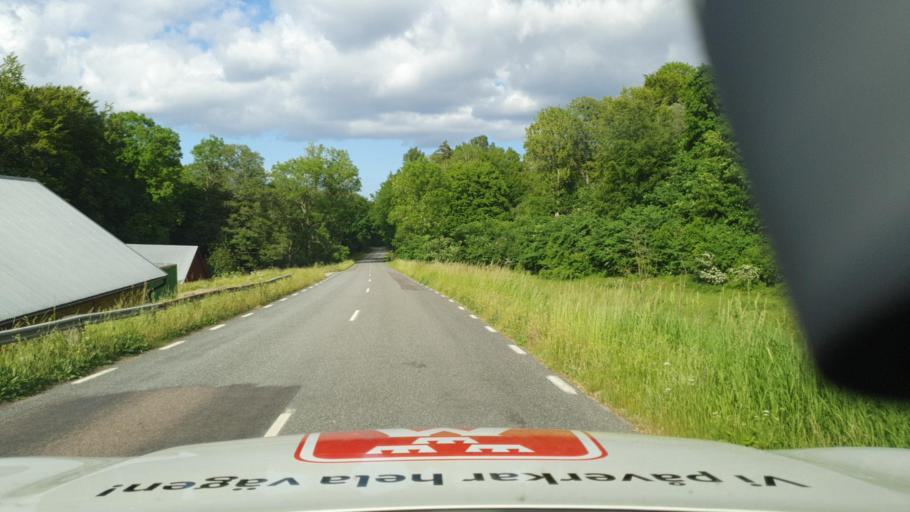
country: SE
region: Skane
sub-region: Simrishamns Kommun
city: Kivik
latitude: 55.6183
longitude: 14.2395
